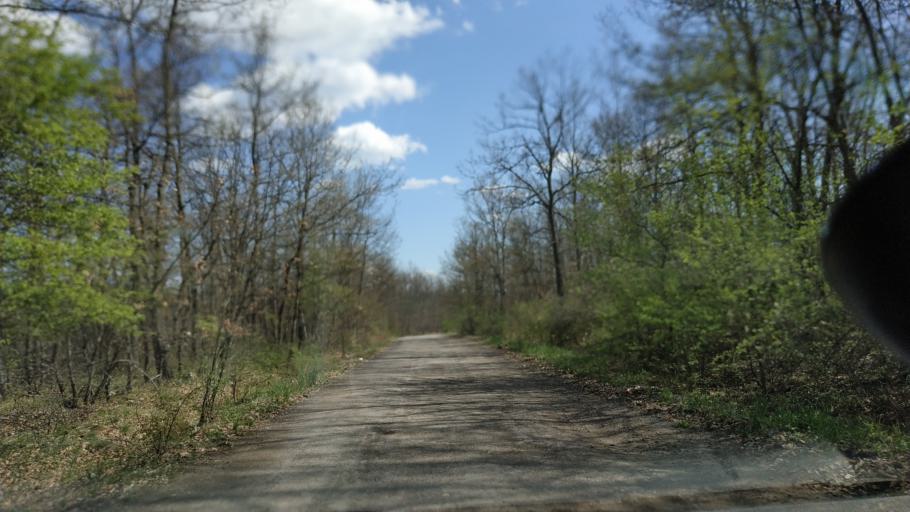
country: RS
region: Central Serbia
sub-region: Zajecarski Okrug
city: Soko Banja
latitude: 43.5380
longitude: 21.9050
